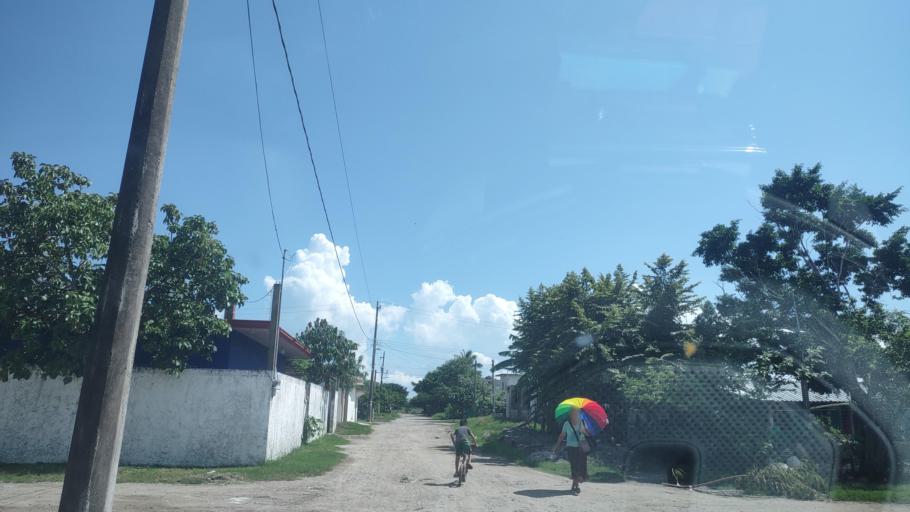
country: MX
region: Veracruz
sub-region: Ozuluama de Mascarenas
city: Cucharas
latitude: 21.6182
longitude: -97.6563
